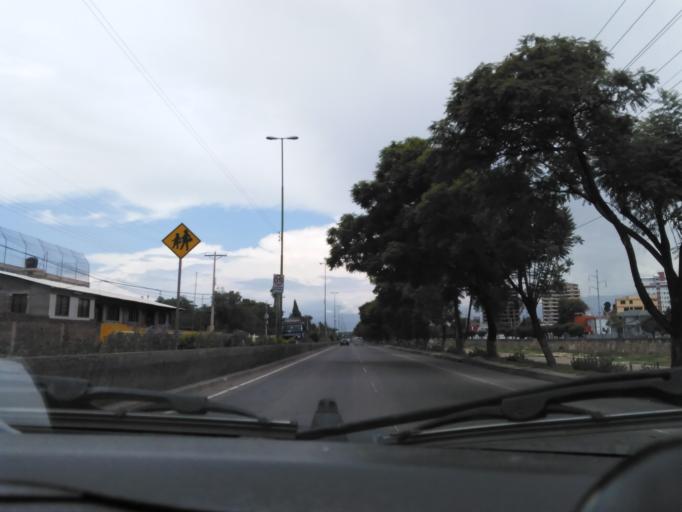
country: BO
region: Cochabamba
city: Cochabamba
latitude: -17.3781
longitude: -66.1453
